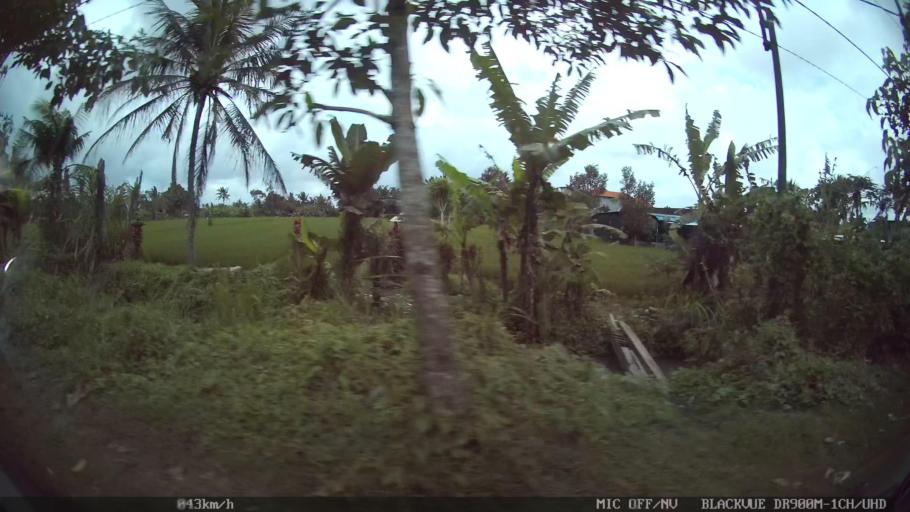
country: ID
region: Bali
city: Banjar Pekenjelodan
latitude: -8.5590
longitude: 115.1890
